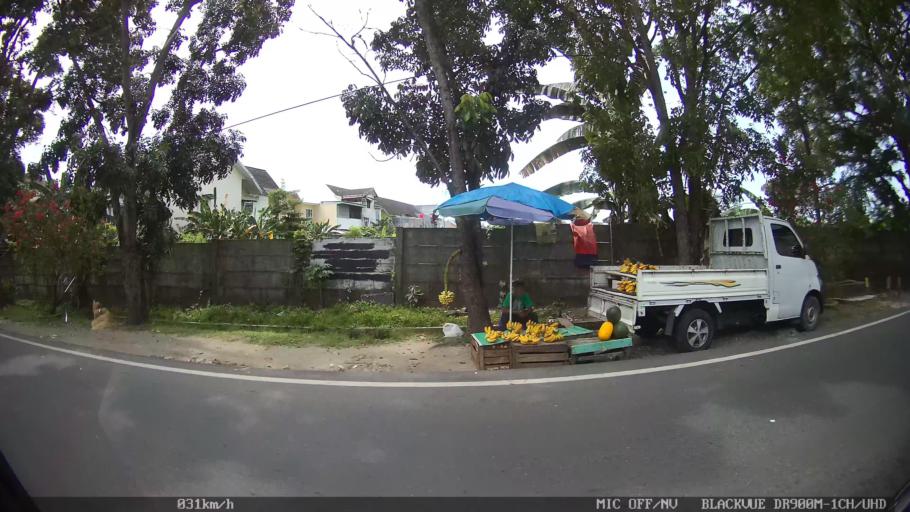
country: ID
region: North Sumatra
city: Sunggal
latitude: 3.5755
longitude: 98.6150
